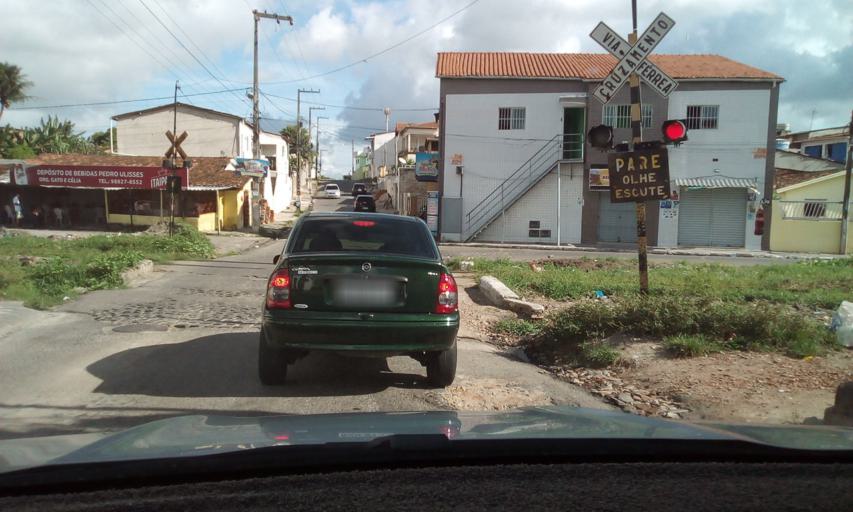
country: BR
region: Paraiba
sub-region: Bayeux
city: Bayeux
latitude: -7.1297
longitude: -34.9216
